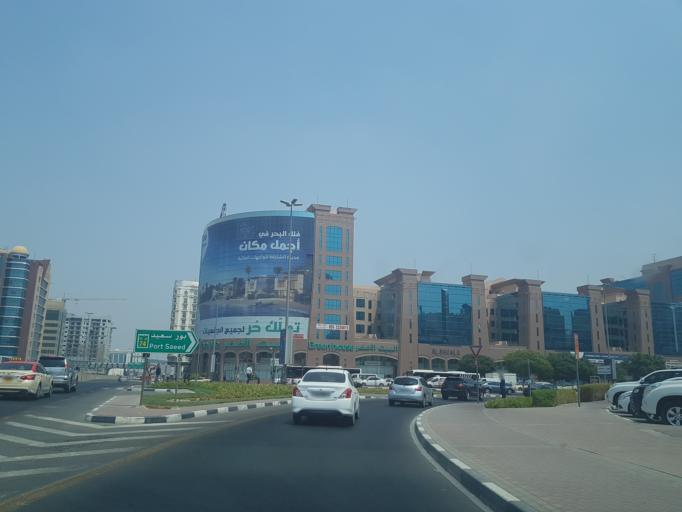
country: AE
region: Ash Shariqah
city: Sharjah
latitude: 25.2576
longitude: 55.3301
